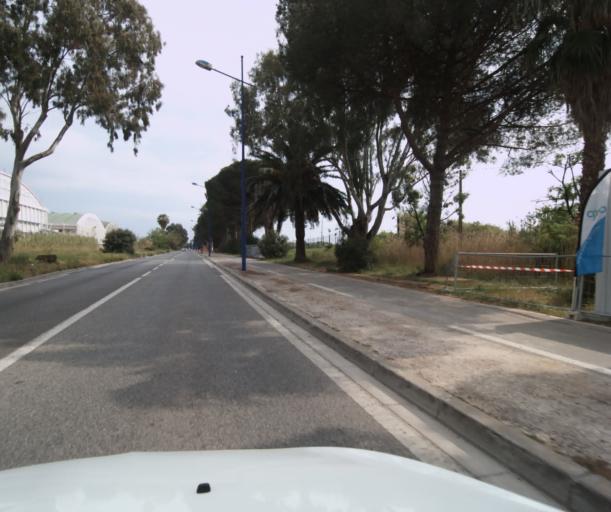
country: FR
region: Provence-Alpes-Cote d'Azur
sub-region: Departement du Var
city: Hyeres
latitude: 43.0910
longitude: 6.1428
